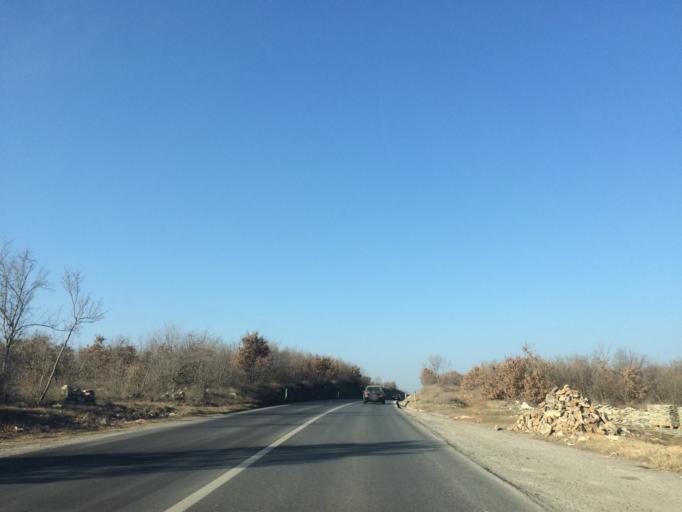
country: XK
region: Pec
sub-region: Komuna e Klines
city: Klina
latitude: 42.5942
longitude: 20.6329
